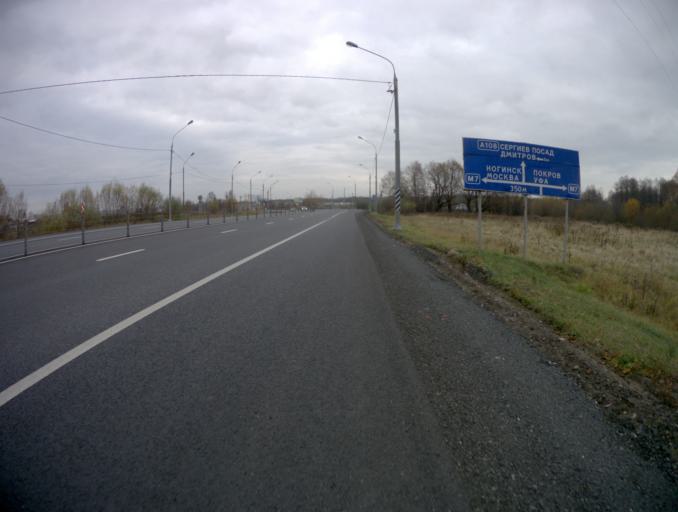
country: RU
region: Moskovskaya
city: Malaya Dubna
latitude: 55.8731
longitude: 38.9633
